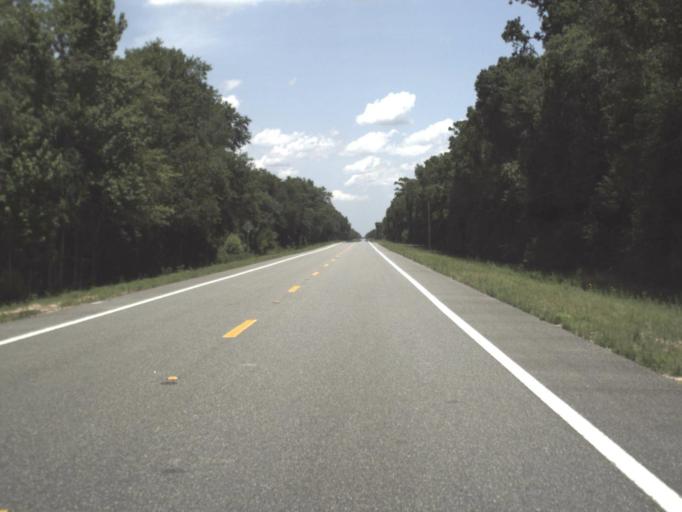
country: US
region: Florida
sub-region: Taylor County
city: Steinhatchee
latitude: 29.7847
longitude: -83.3227
